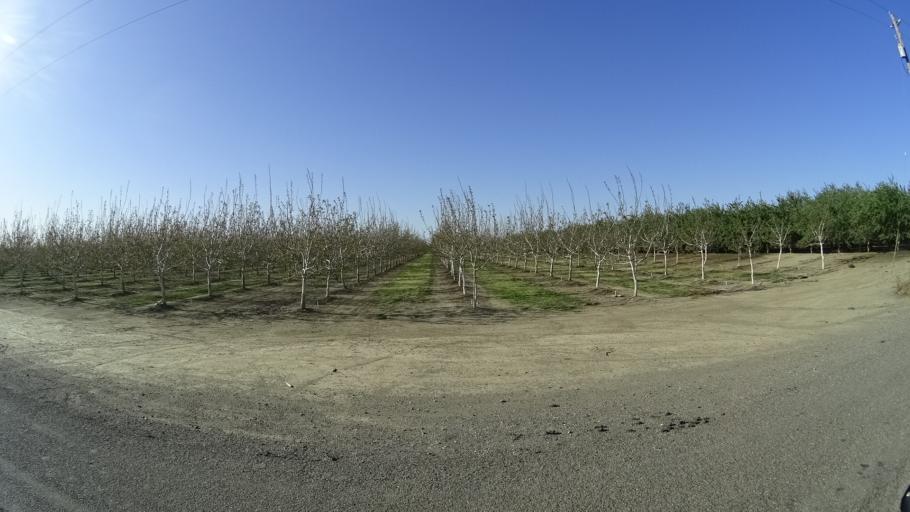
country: US
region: California
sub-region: Glenn County
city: Orland
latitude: 39.7146
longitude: -122.1617
